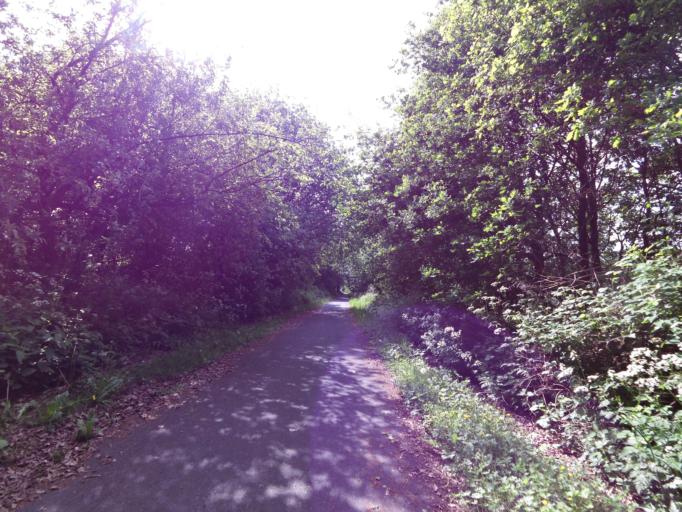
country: BE
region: Flanders
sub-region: Provincie West-Vlaanderen
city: Beernem
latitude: 51.1407
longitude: 3.3161
